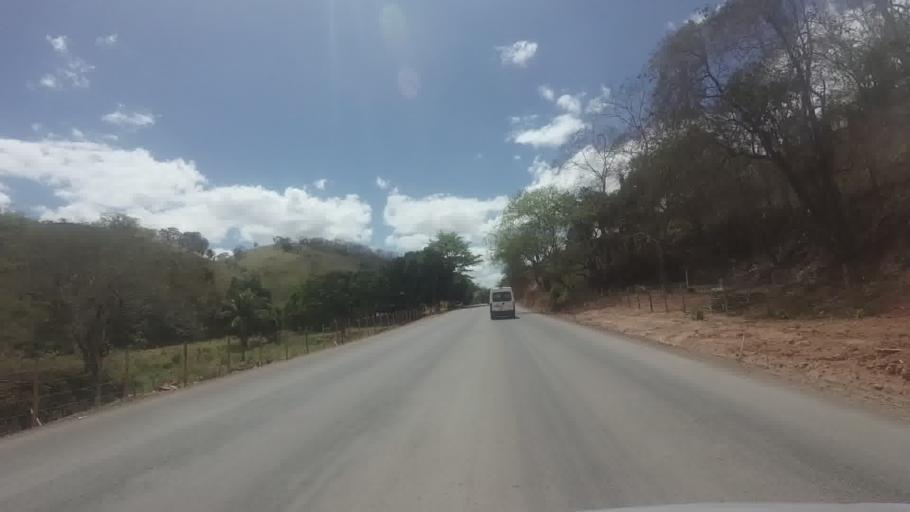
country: BR
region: Rio de Janeiro
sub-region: Santo Antonio De Padua
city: Santo Antonio de Padua
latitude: -21.5042
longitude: -42.0816
